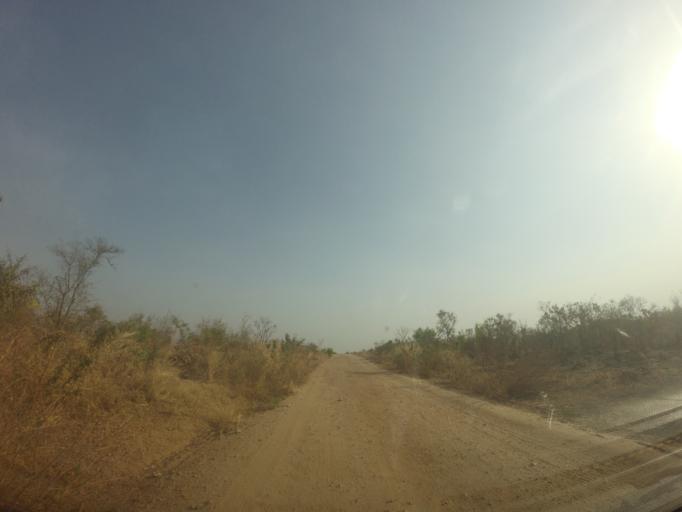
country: UG
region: Northern Region
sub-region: Maracha District
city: Maracha
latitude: 3.1146
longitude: 31.1568
